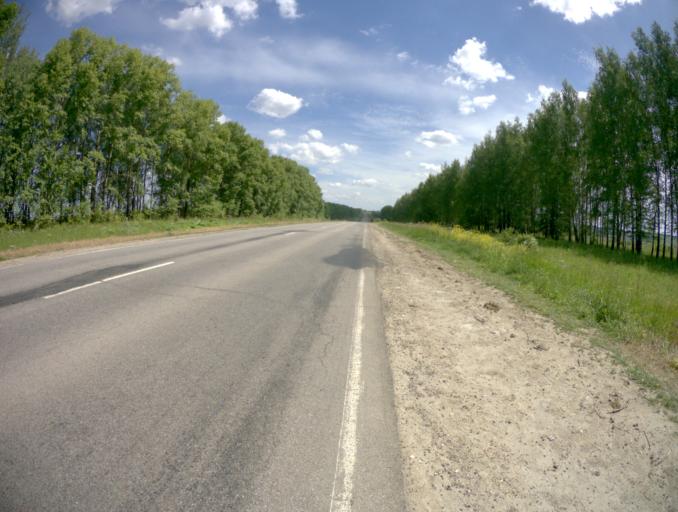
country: RU
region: Ivanovo
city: Gavrilov Posad
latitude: 56.3790
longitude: 40.0150
